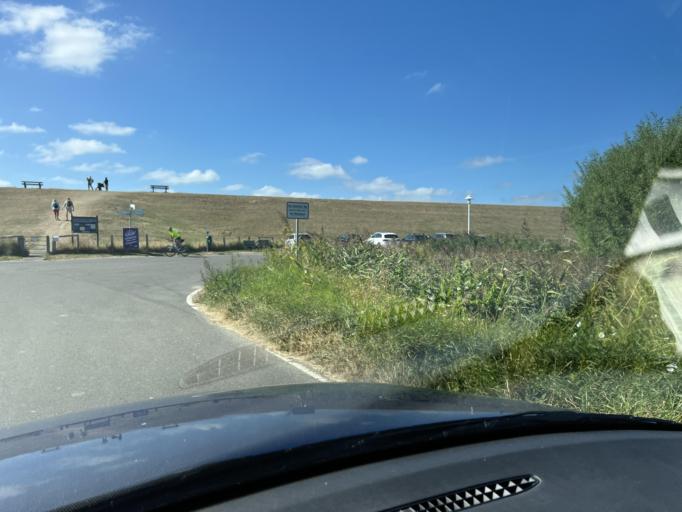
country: DE
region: Schleswig-Holstein
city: Wesselburenerkoog
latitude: 54.2475
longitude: 8.8415
